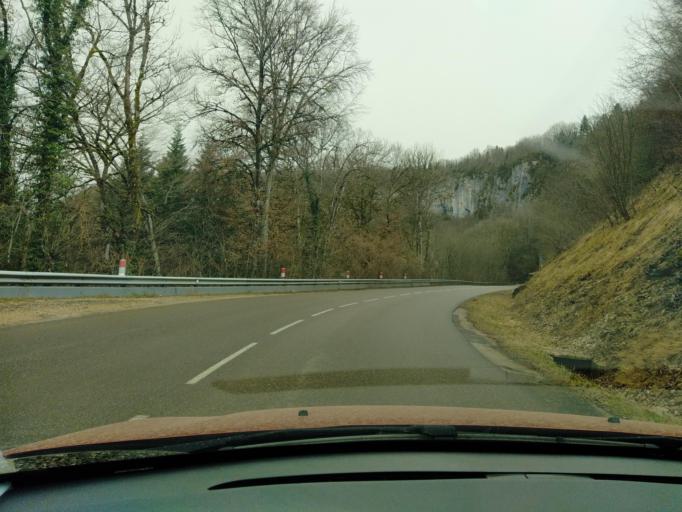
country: FR
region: Franche-Comte
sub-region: Departement du Jura
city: Clairvaux-les-Lacs
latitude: 46.6343
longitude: 5.7489
